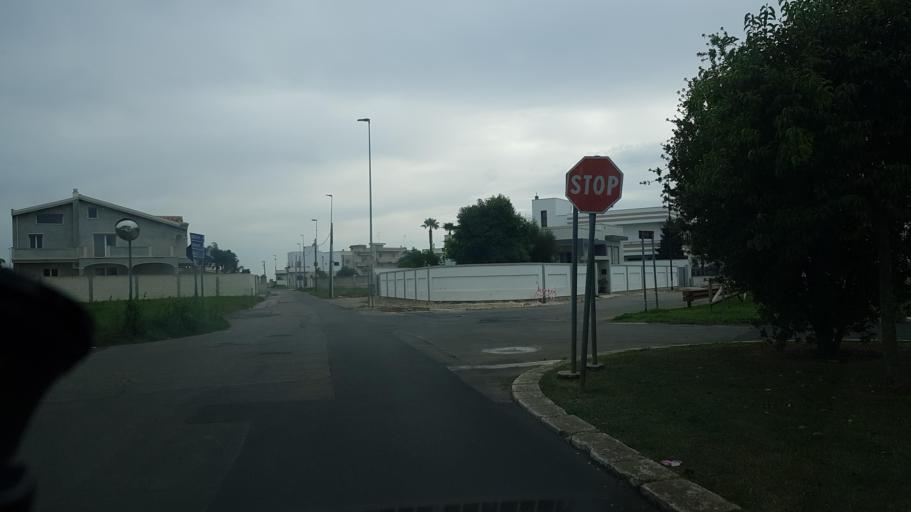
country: IT
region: Apulia
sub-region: Provincia di Lecce
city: Leverano
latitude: 40.2863
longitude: 18.0048
